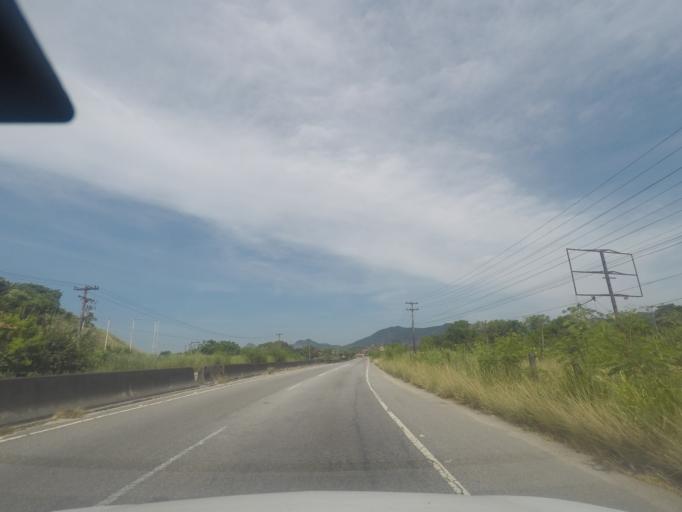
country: BR
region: Rio de Janeiro
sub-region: Marica
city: Marica
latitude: -22.9058
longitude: -42.8120
